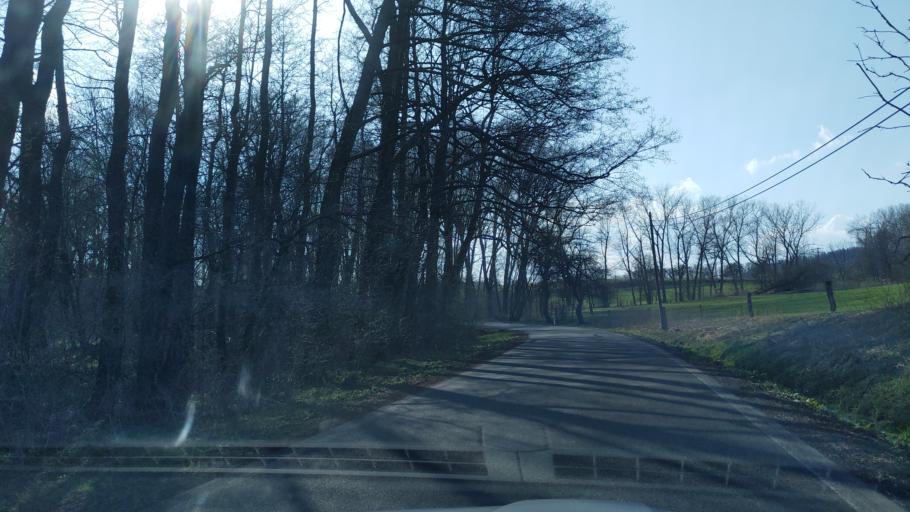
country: CZ
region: Ustecky
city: Vernerice
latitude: 50.6826
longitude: 14.3147
